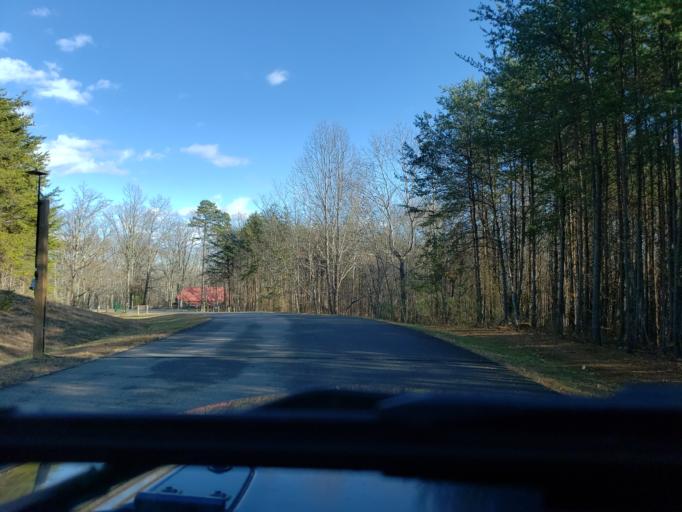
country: US
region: North Carolina
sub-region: Cleveland County
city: White Plains
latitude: 35.1707
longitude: -81.3635
